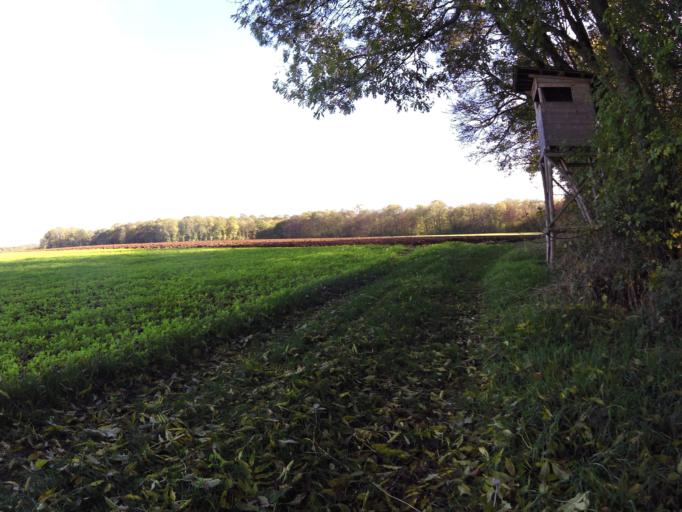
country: DE
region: Bavaria
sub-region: Regierungsbezirk Unterfranken
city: Sulzfeld am Main
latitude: 49.7230
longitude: 10.0927
